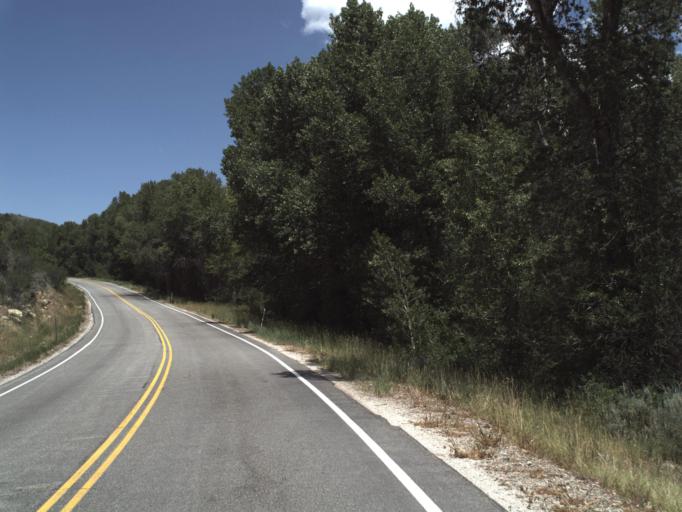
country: US
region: Utah
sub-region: Weber County
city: Wolf Creek
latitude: 41.3480
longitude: -111.5973
